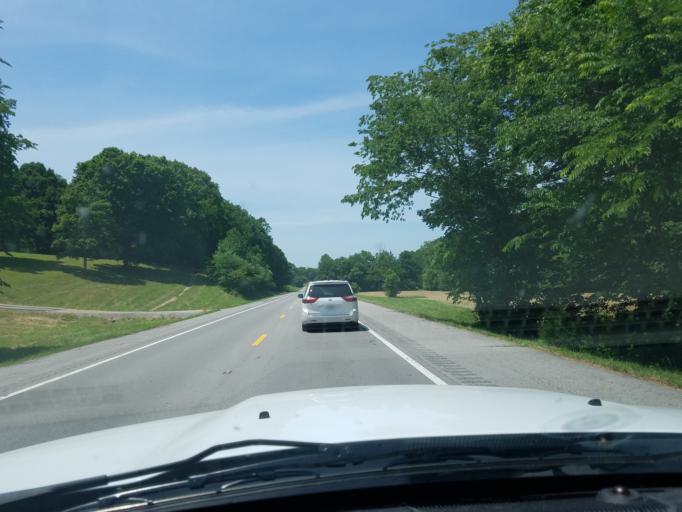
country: US
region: Tennessee
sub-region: Sumner County
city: Westmoreland
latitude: 36.6145
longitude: -86.2346
